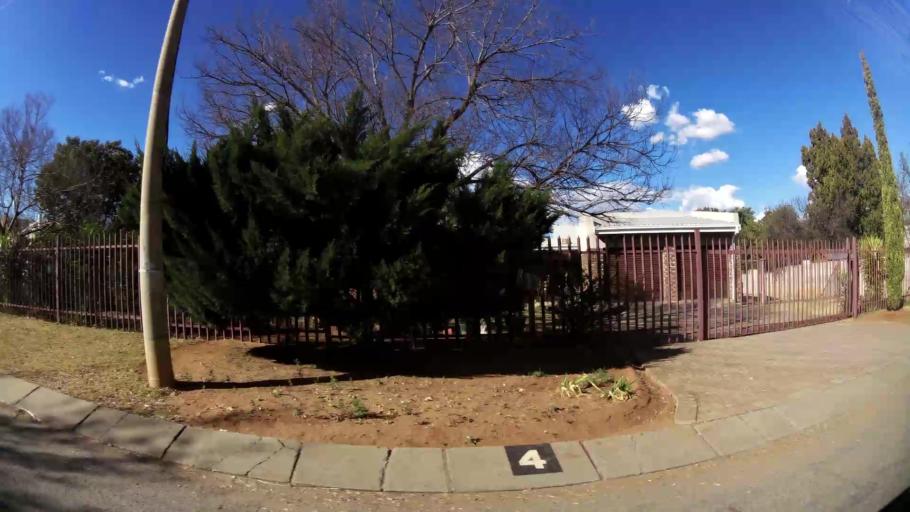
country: ZA
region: North-West
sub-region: Dr Kenneth Kaunda District Municipality
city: Klerksdorp
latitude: -26.8279
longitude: 26.6628
